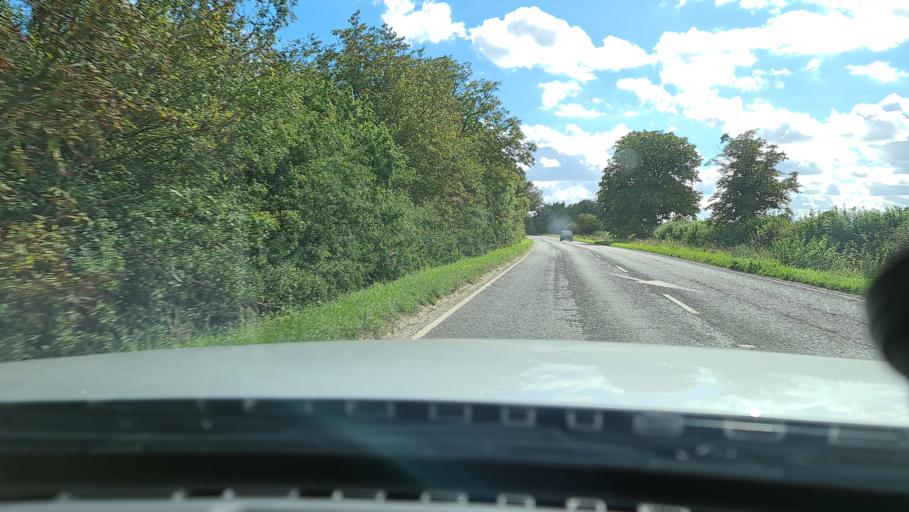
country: GB
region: England
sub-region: Oxfordshire
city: Somerton
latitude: 51.9186
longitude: -1.2224
